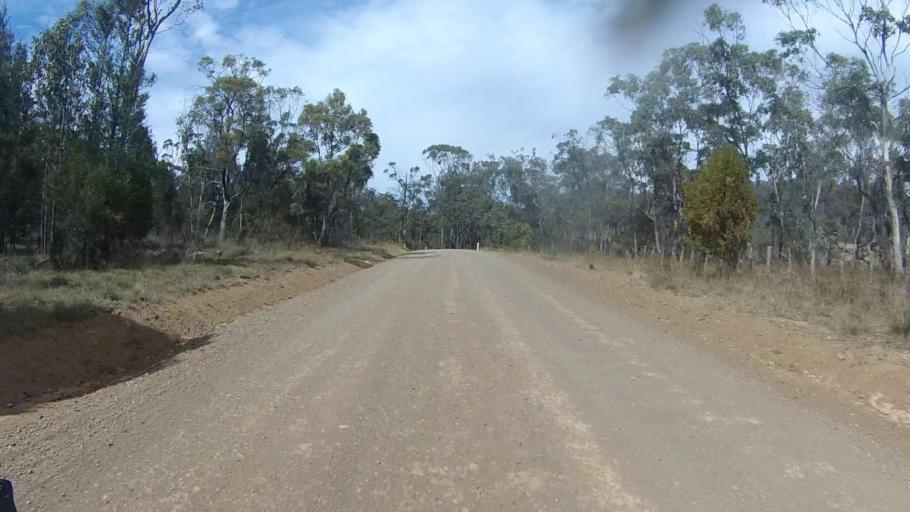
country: AU
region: Tasmania
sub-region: Sorell
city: Sorell
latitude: -42.6490
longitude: 147.8991
